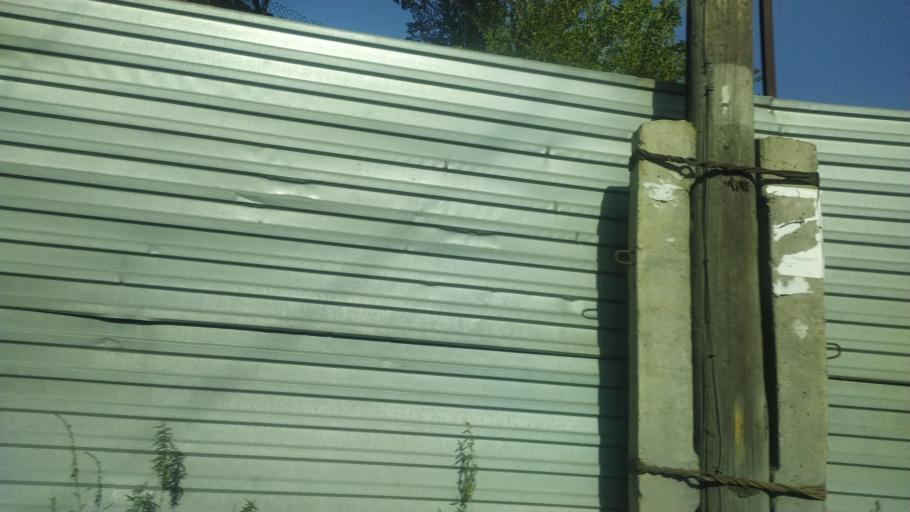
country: KZ
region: Almaty Qalasy
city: Almaty
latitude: 43.2670
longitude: 76.8736
